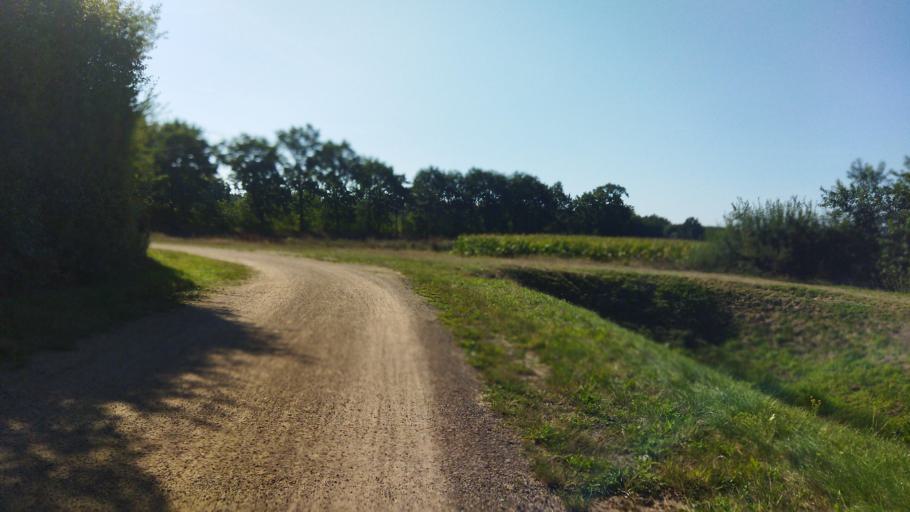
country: DE
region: Lower Saxony
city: Haren
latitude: 52.7724
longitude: 7.2701
